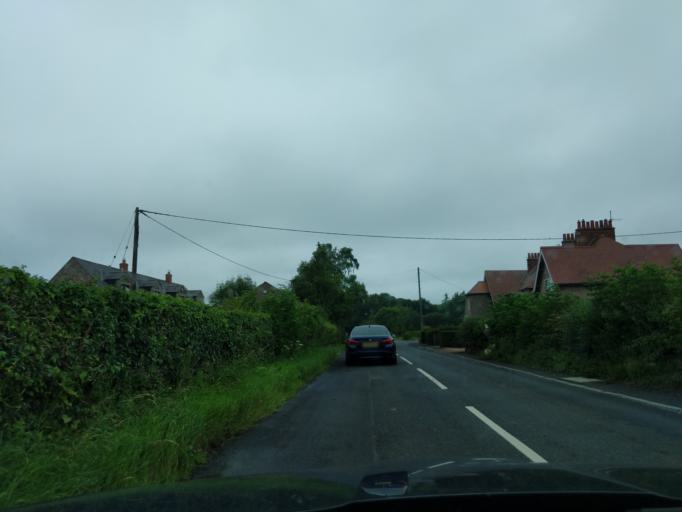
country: GB
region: England
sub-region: Northumberland
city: Lowick
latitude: 55.6506
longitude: -1.9963
